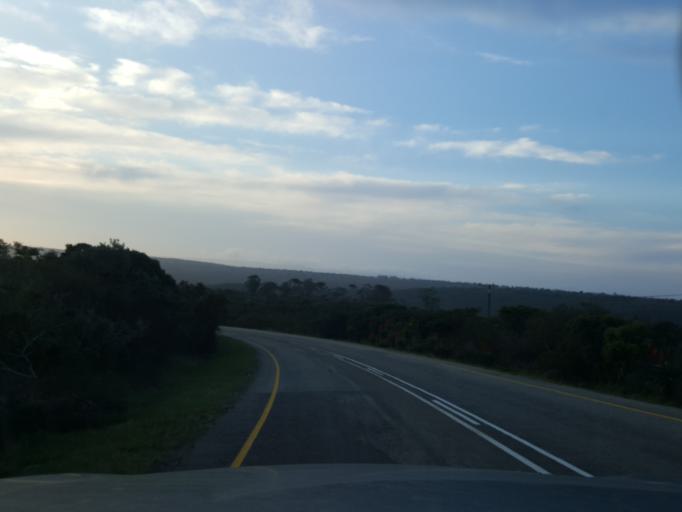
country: ZA
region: Eastern Cape
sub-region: Cacadu District Municipality
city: Grahamstown
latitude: -33.4789
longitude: 26.4896
